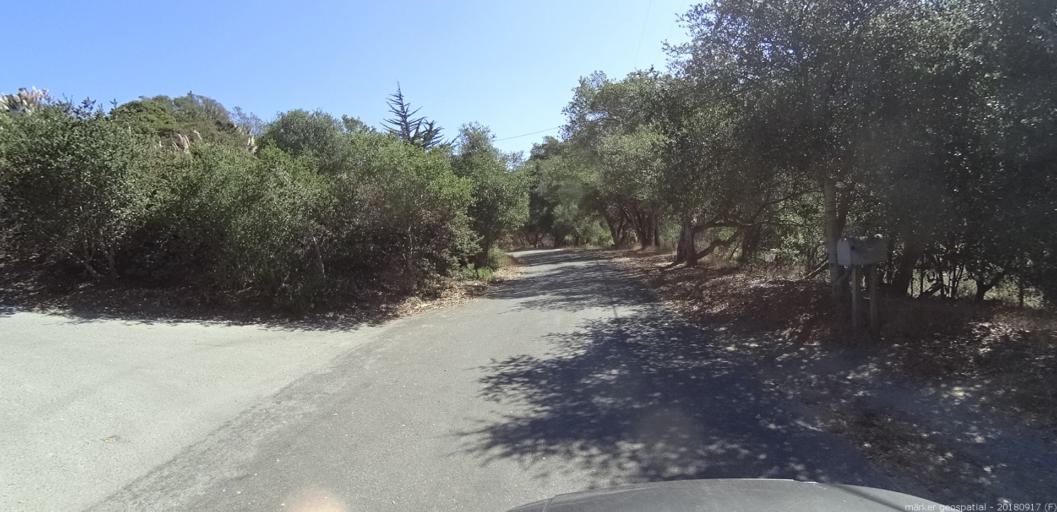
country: US
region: California
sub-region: Monterey County
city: Elkhorn
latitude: 36.8300
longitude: -121.6941
